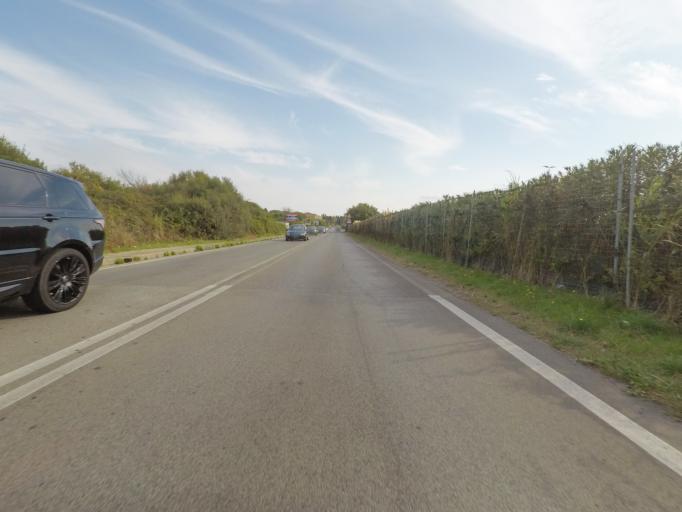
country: IT
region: Latium
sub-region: Citta metropolitana di Roma Capitale
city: Civitavecchia
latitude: 42.0635
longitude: 11.8145
